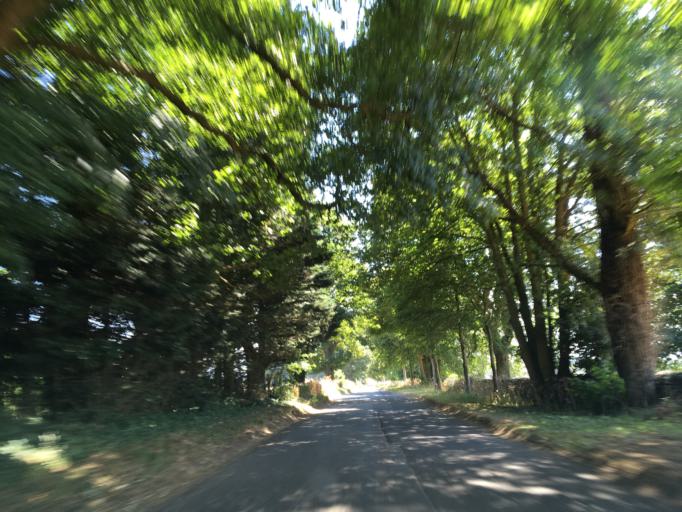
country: GB
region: England
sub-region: Gloucestershire
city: Coates
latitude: 51.6772
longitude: -2.0860
